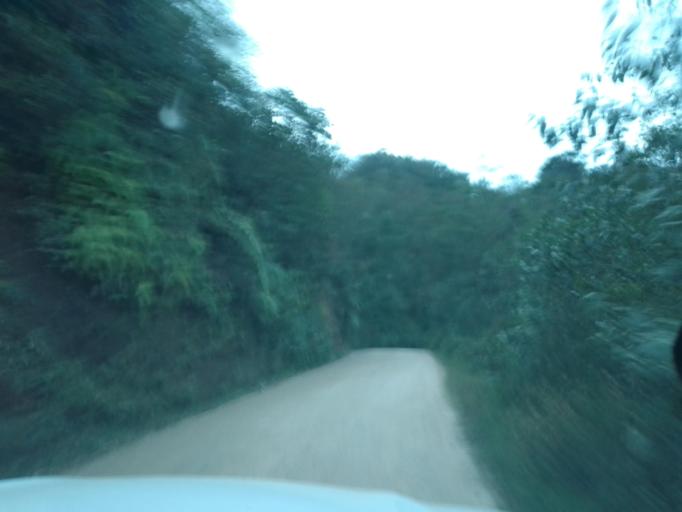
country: MX
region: Chiapas
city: Motozintla de Mendoza
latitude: 15.2238
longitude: -92.2372
